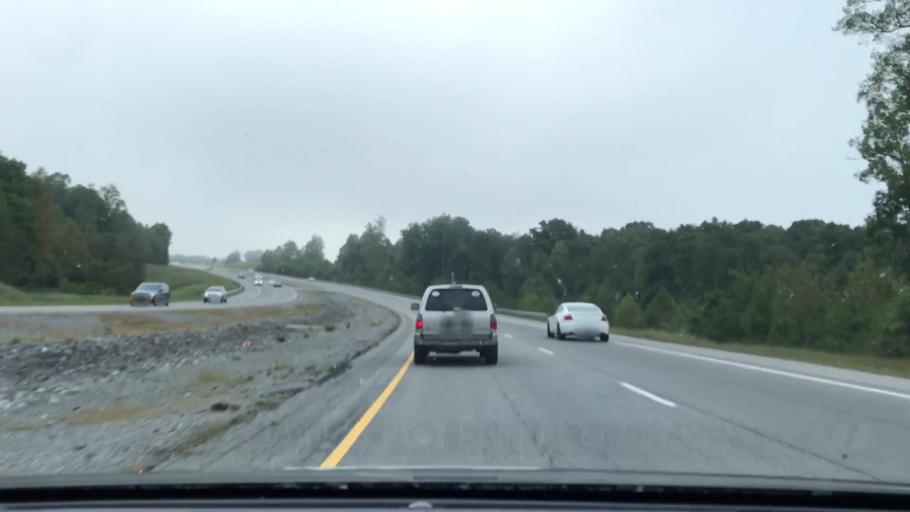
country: US
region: Tennessee
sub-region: Sumner County
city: Portland
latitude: 36.4858
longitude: -86.4833
